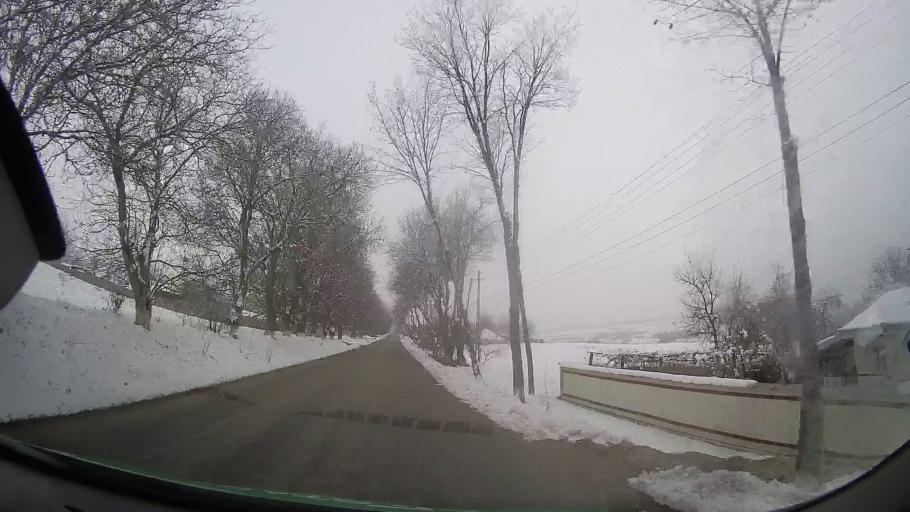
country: RO
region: Bacau
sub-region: Comuna Oncesti
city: Oncesti
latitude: 46.4388
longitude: 27.2673
